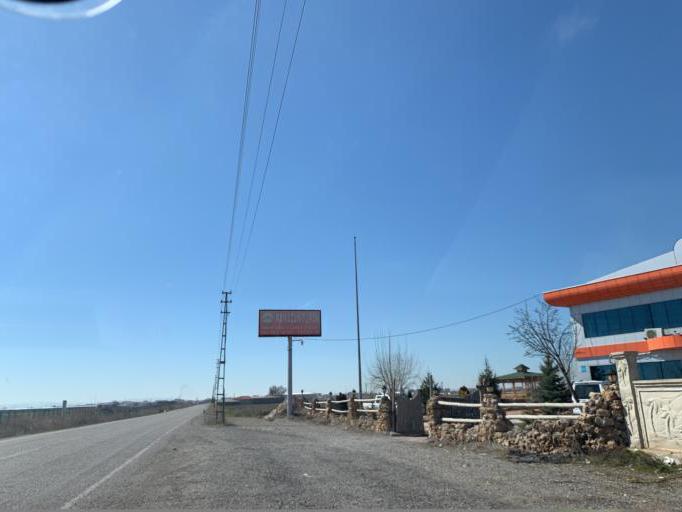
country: TR
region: Konya
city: Cumra
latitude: 37.5966
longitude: 32.7902
